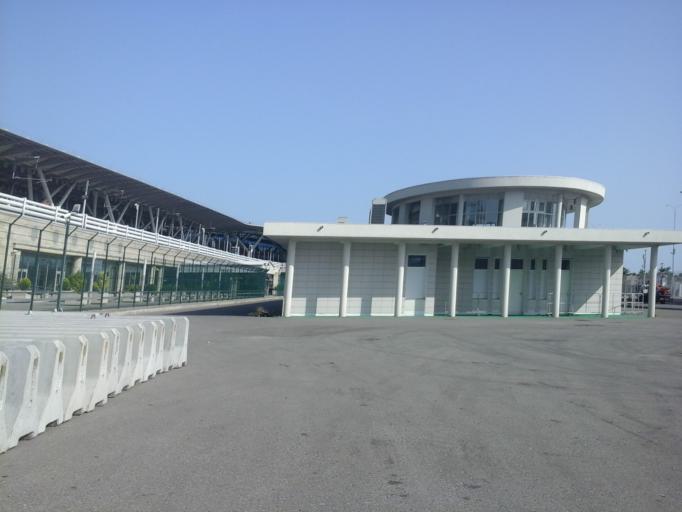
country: RU
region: Krasnodarskiy
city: Adler
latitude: 43.4124
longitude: 39.9710
